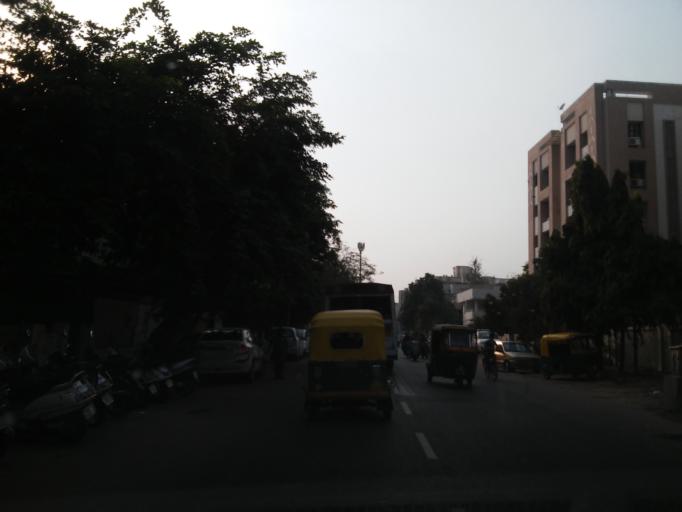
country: IN
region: Gujarat
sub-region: Ahmadabad
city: Ahmedabad
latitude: 23.0098
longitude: 72.5546
